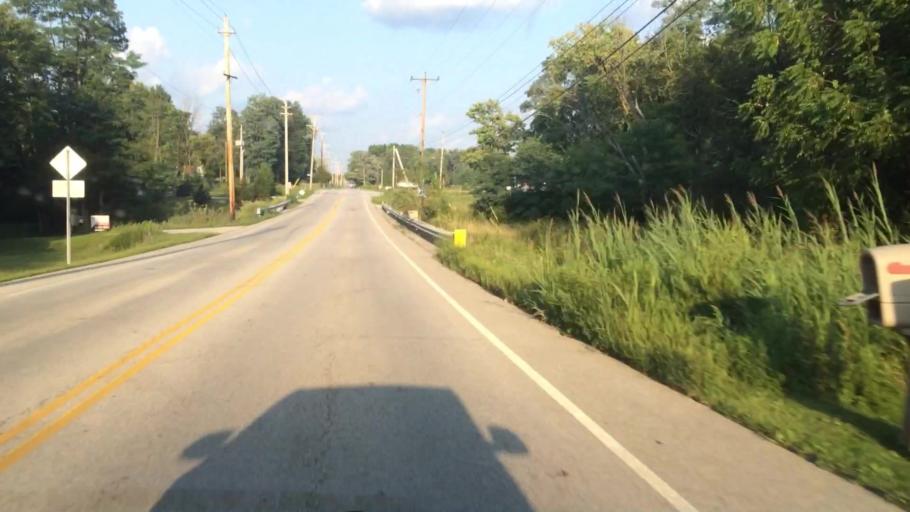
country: US
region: Ohio
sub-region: Summit County
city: Silver Lake
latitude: 41.2027
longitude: -81.4742
